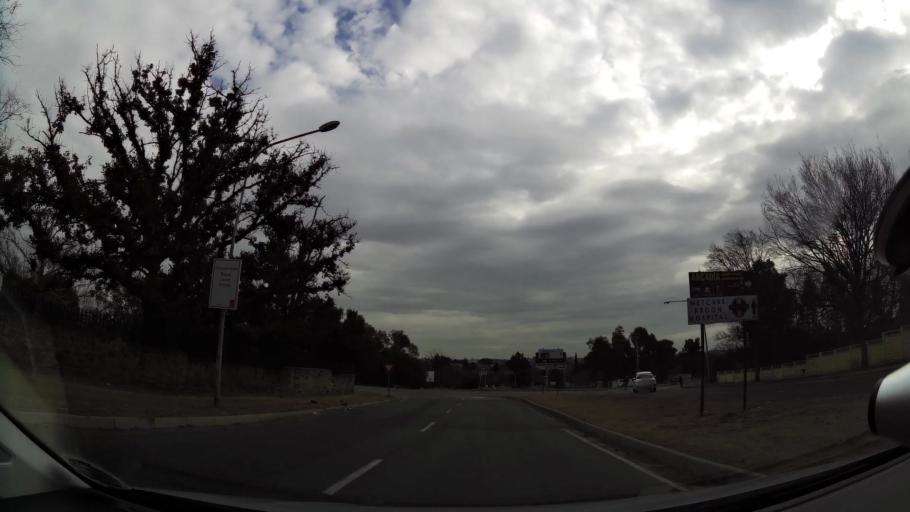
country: ZA
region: Orange Free State
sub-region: Fezile Dabi District Municipality
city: Kroonstad
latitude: -27.6741
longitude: 27.2389
